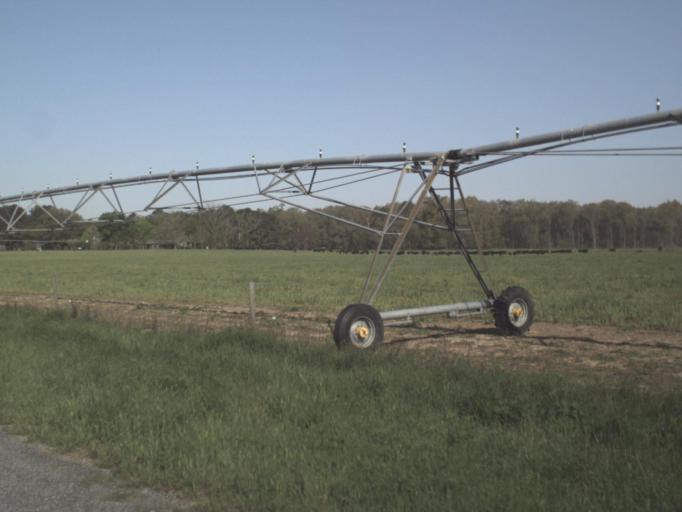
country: US
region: Florida
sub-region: Jackson County
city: Malone
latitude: 30.9759
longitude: -85.0454
